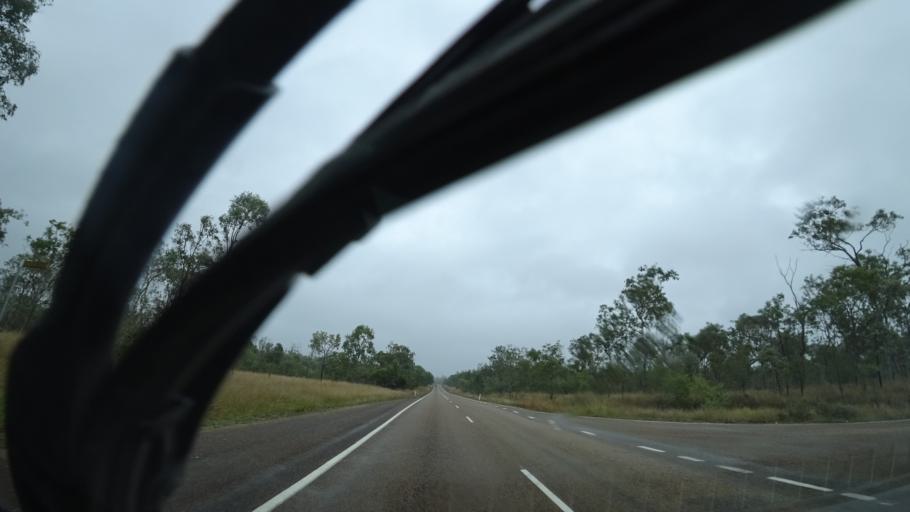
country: AU
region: Queensland
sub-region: Tablelands
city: Ravenshoe
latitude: -17.6941
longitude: 145.2187
